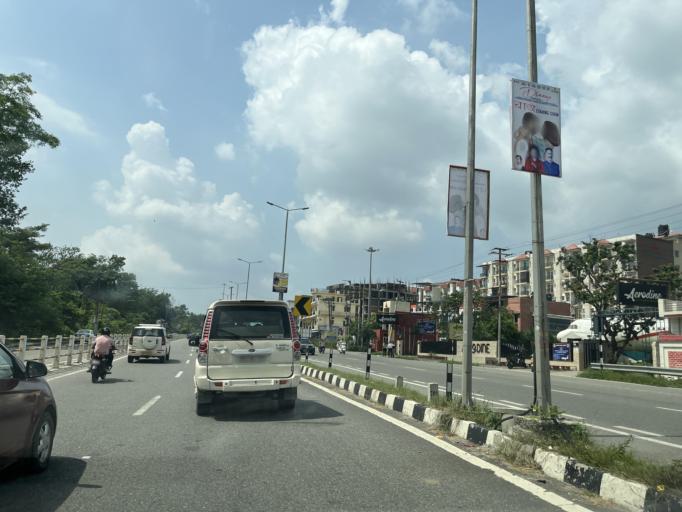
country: IN
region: Uttarakhand
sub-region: Dehradun
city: Raipur
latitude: 30.2709
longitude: 78.0795
